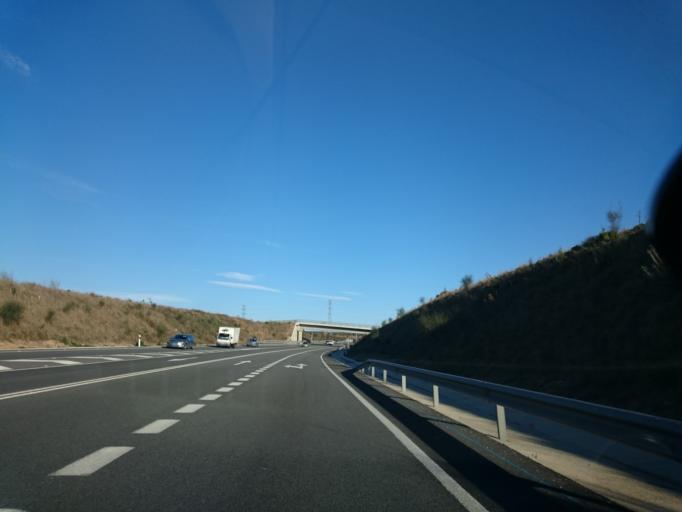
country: ES
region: Catalonia
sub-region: Provincia de Barcelona
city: Vilafranca del Penedes
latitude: 41.3556
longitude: 1.7216
